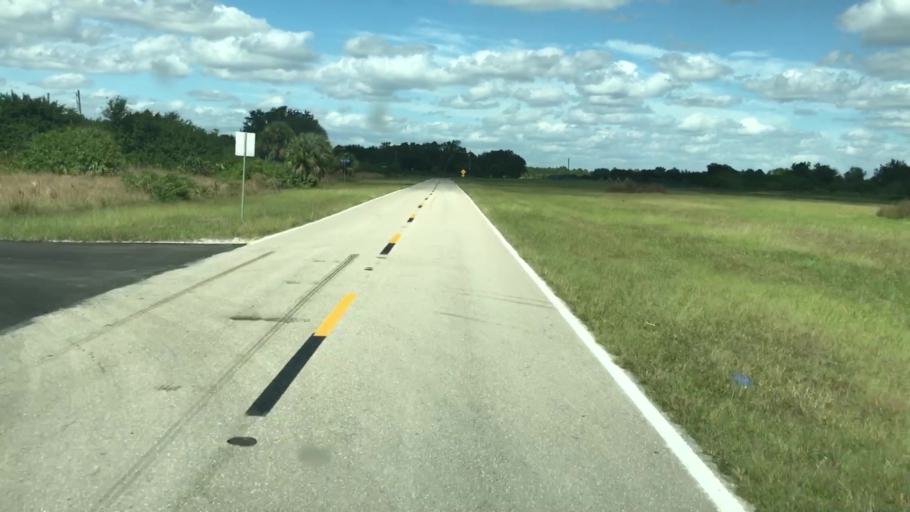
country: US
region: Florida
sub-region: Lee County
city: Olga
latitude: 26.6829
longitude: -81.6637
